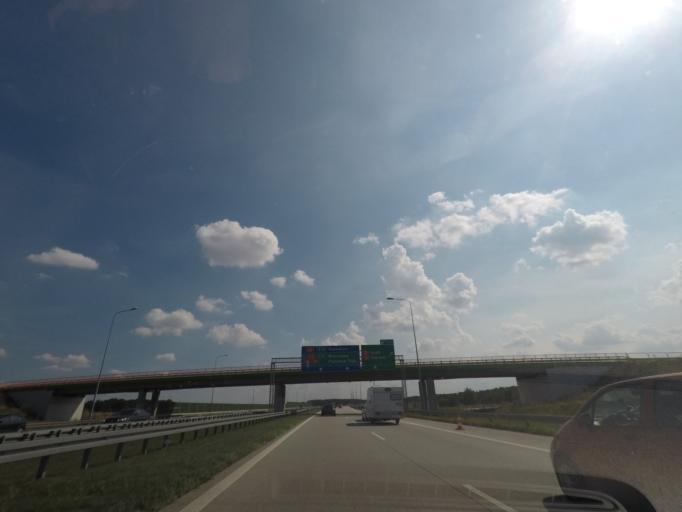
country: PL
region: Lodz Voivodeship
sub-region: Powiat piotrkowski
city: Czarnocin
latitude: 51.5558
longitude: 19.6043
